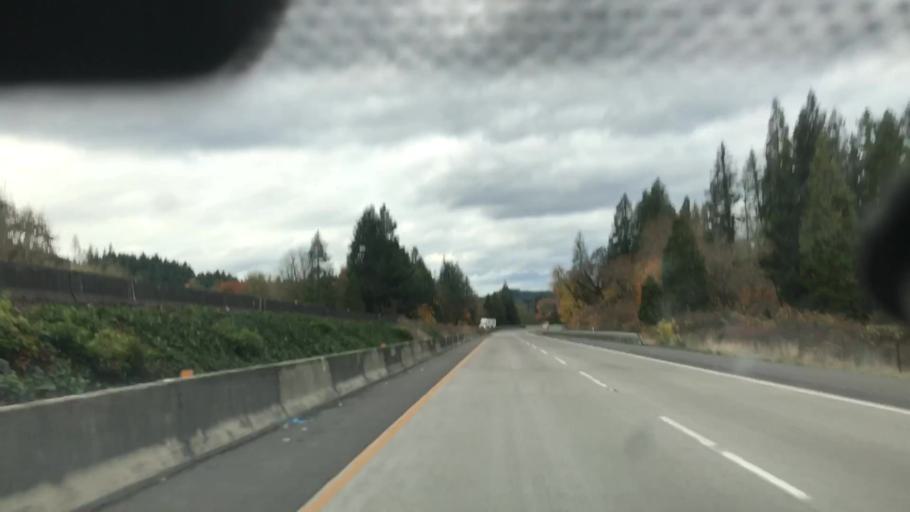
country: US
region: Oregon
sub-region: Douglas County
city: Yoncalla
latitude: 43.6249
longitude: -123.2175
